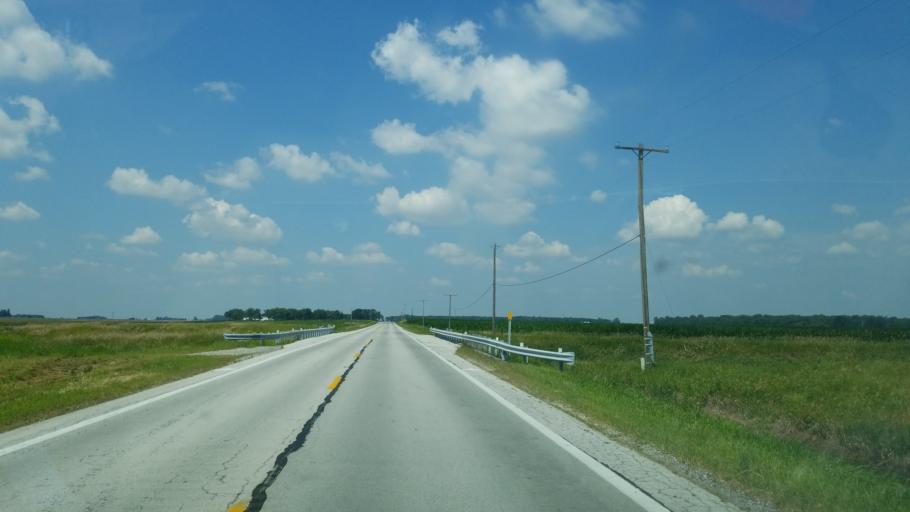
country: US
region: Ohio
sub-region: Wood County
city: North Baltimore
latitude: 41.2836
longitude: -83.7019
